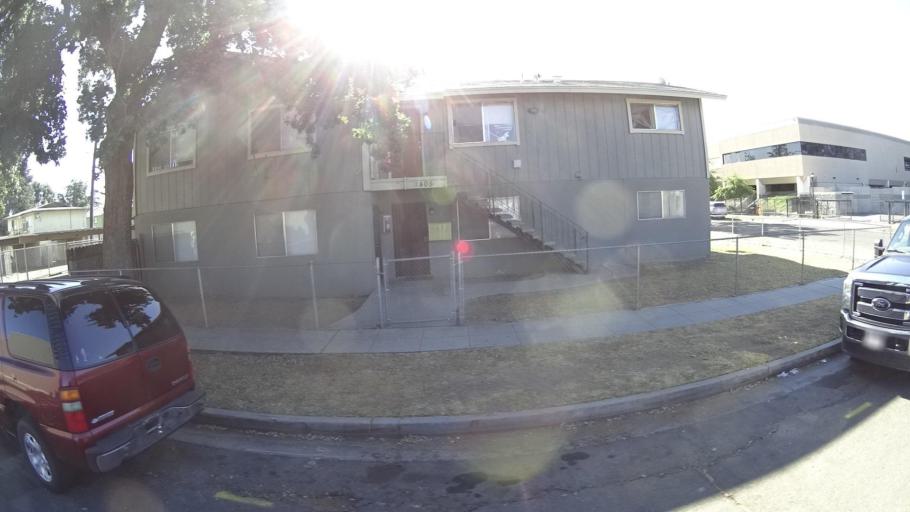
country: US
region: California
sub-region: Fresno County
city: Fresno
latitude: 36.7697
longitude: -119.7946
